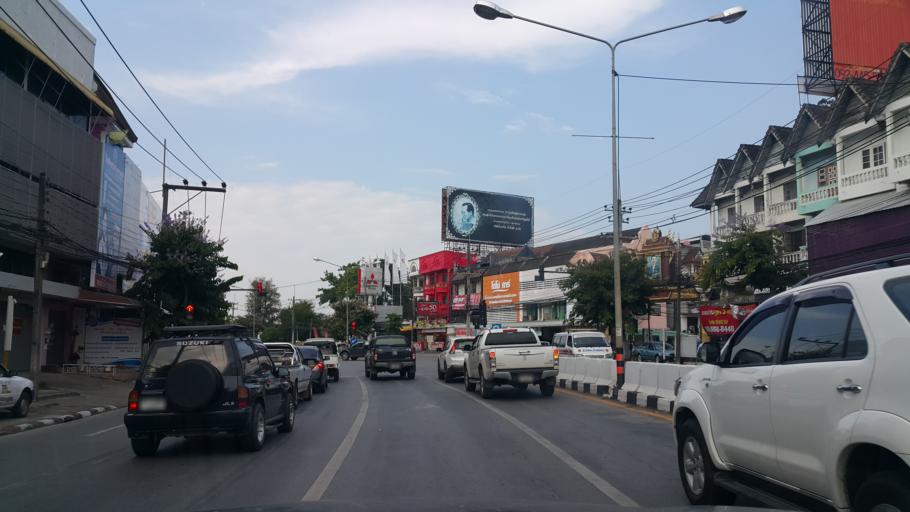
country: TH
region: Chiang Rai
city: Chiang Rai
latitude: 19.9152
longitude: 99.8460
